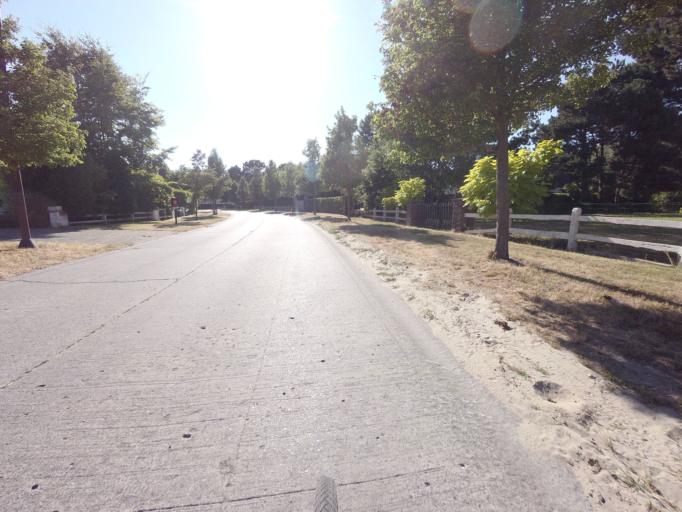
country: BE
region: Flanders
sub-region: Provincie West-Vlaanderen
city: De Haan
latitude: 51.2665
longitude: 3.0197
